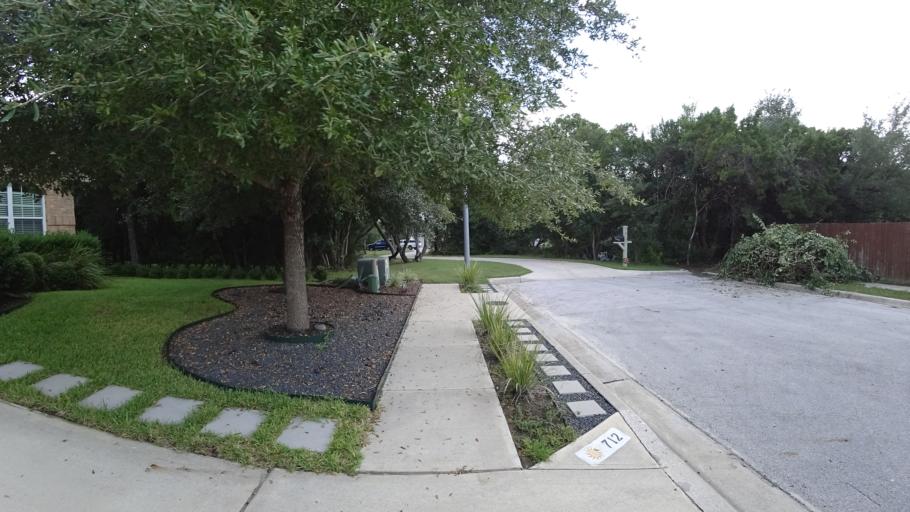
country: US
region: Texas
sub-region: Travis County
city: Onion Creek
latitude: 30.1889
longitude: -97.7983
